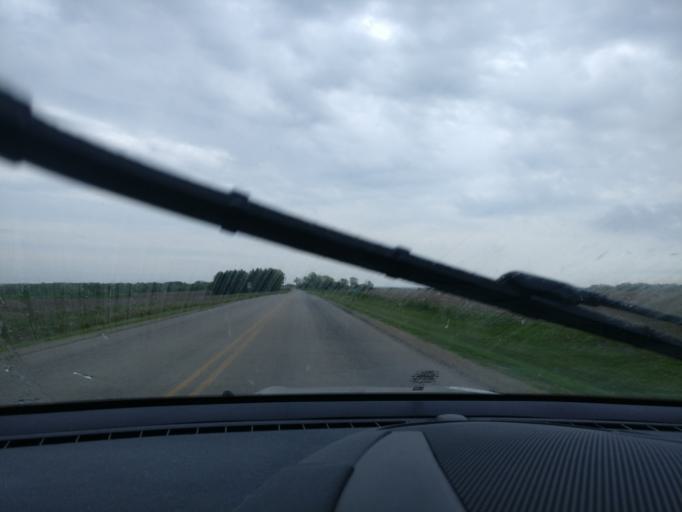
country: US
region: Wisconsin
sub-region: Lafayette County
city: Darlington
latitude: 42.7521
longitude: -90.0099
